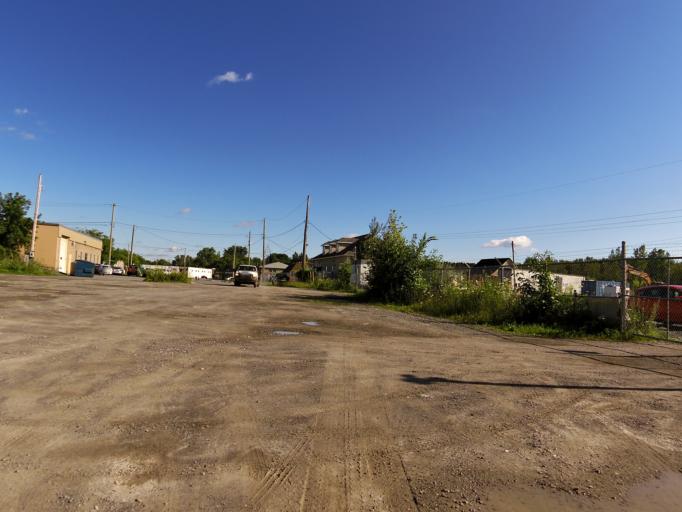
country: CA
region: Ontario
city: Ottawa
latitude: 45.3272
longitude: -75.7259
